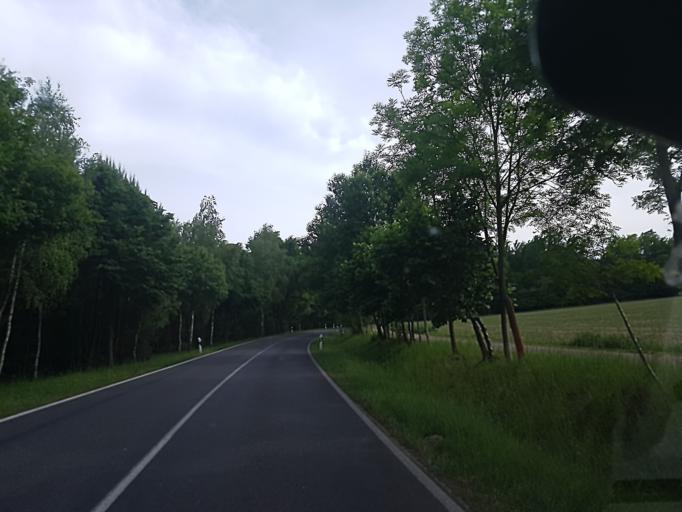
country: DE
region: Brandenburg
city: Belzig
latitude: 52.0376
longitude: 12.5770
